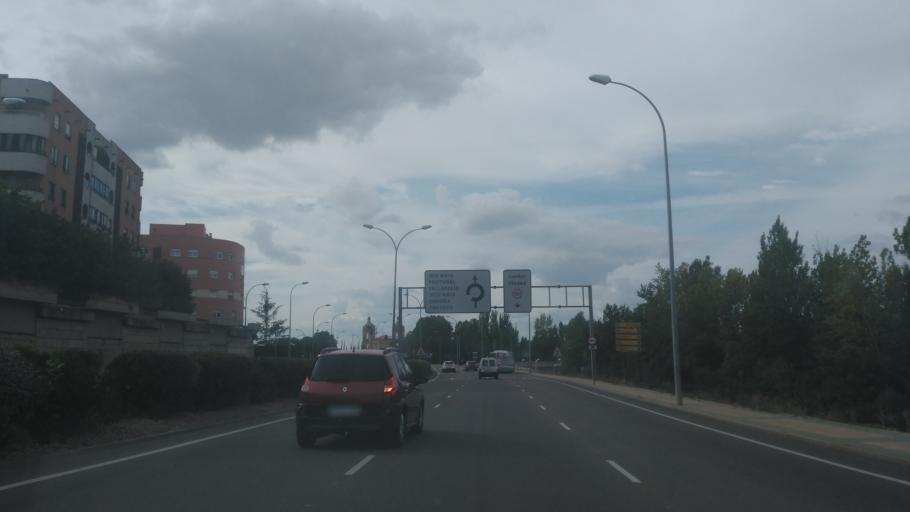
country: ES
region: Castille and Leon
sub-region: Provincia de Salamanca
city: Salamanca
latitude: 40.9536
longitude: -5.6643
